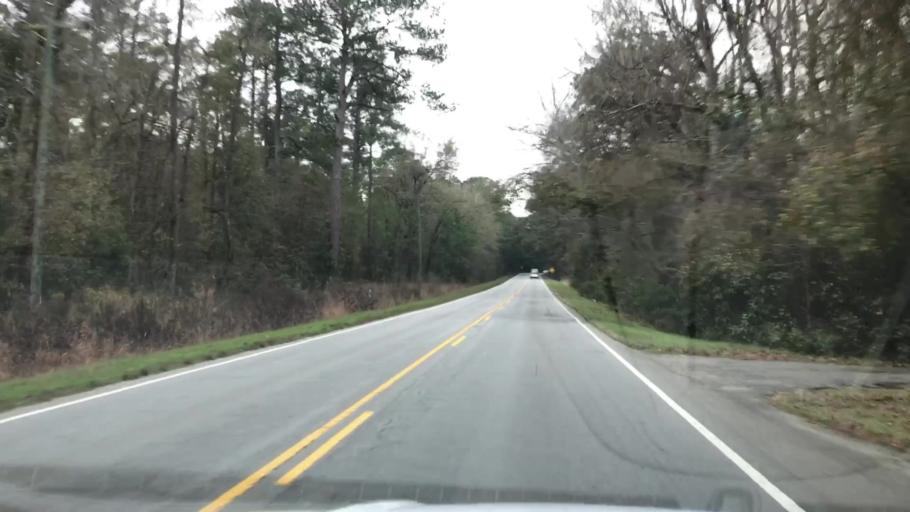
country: US
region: South Carolina
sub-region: Jasper County
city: Ridgeland
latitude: 32.3912
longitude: -80.9075
